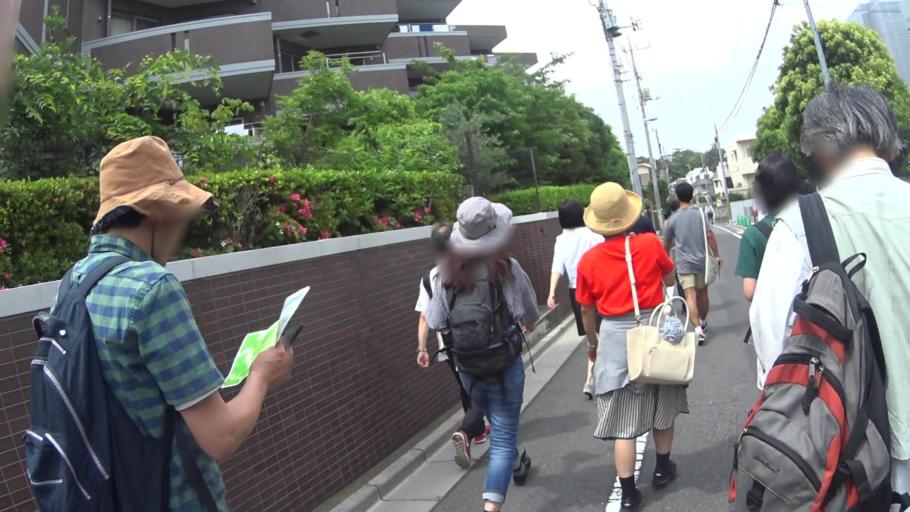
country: JP
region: Tokyo
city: Musashino
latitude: 35.7076
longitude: 139.6056
